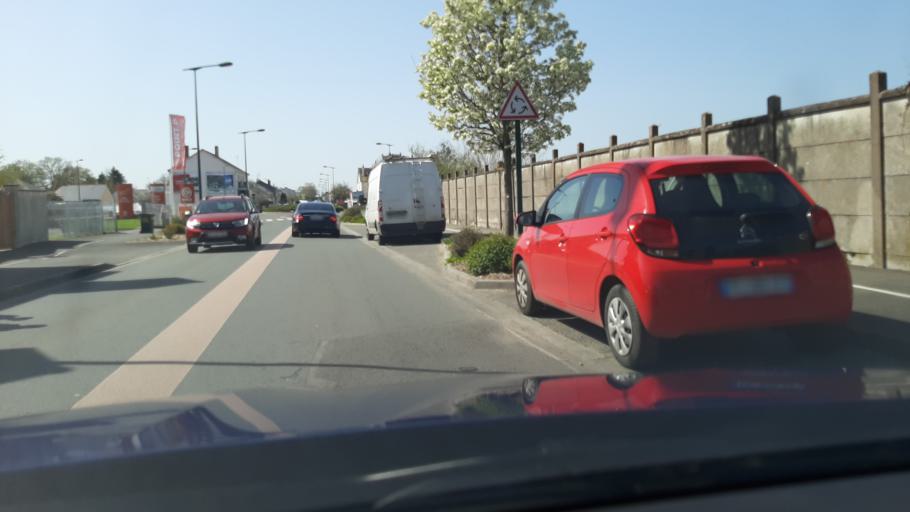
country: FR
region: Pays de la Loire
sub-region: Departement de Maine-et-Loire
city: Les Ponts-de-Ce
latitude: 47.4402
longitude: -0.5013
